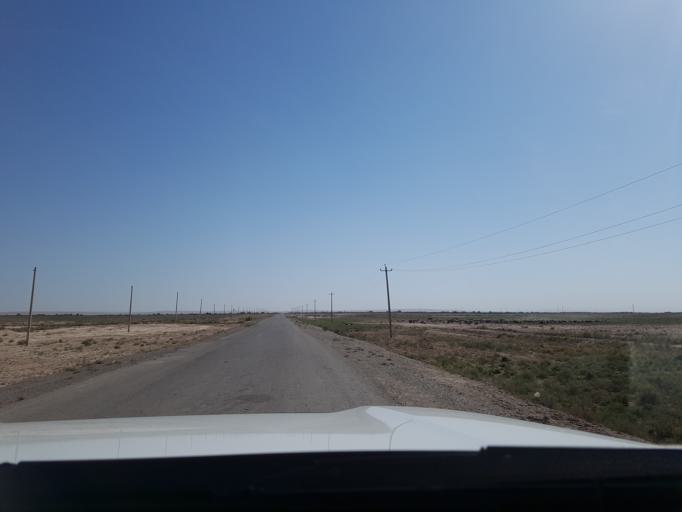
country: IR
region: Razavi Khorasan
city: Sarakhs
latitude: 36.5053
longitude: 61.2533
